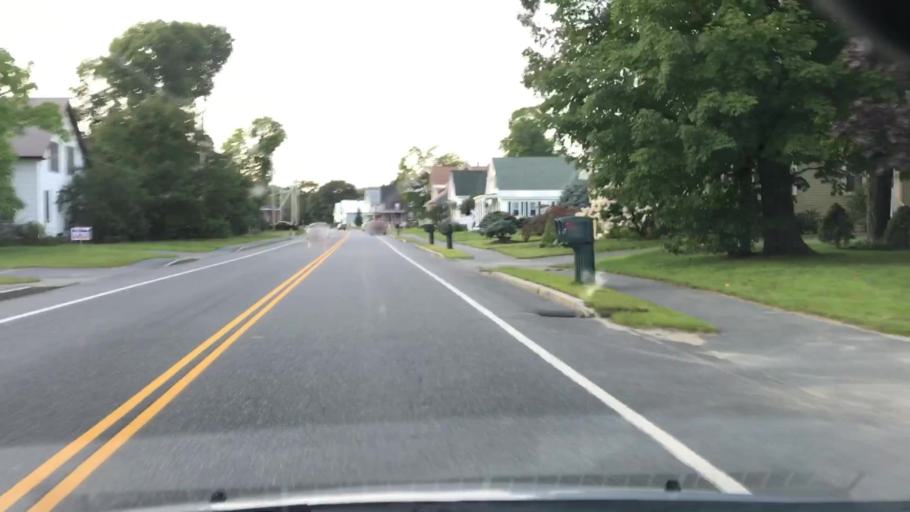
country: US
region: New Hampshire
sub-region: Grafton County
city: Rumney
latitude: 43.9171
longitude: -71.8883
